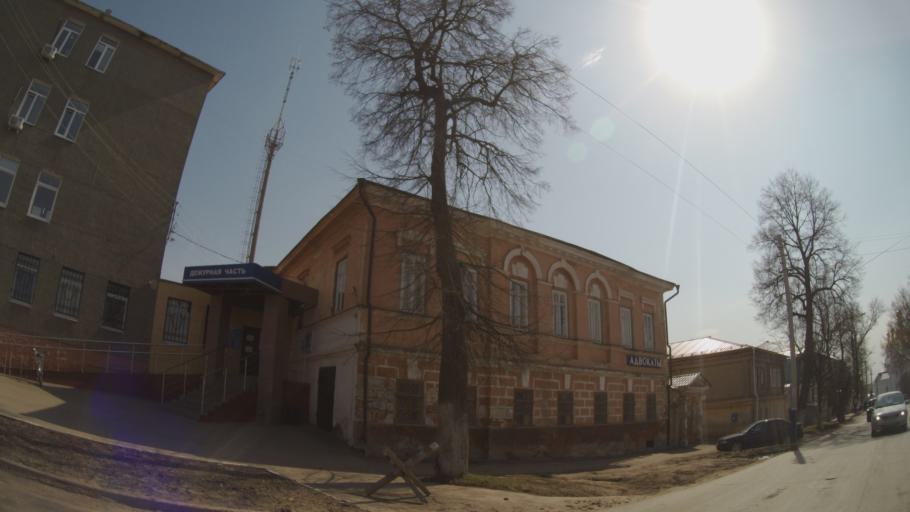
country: RU
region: Nizjnij Novgorod
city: Arzamas
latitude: 55.3869
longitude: 43.8194
